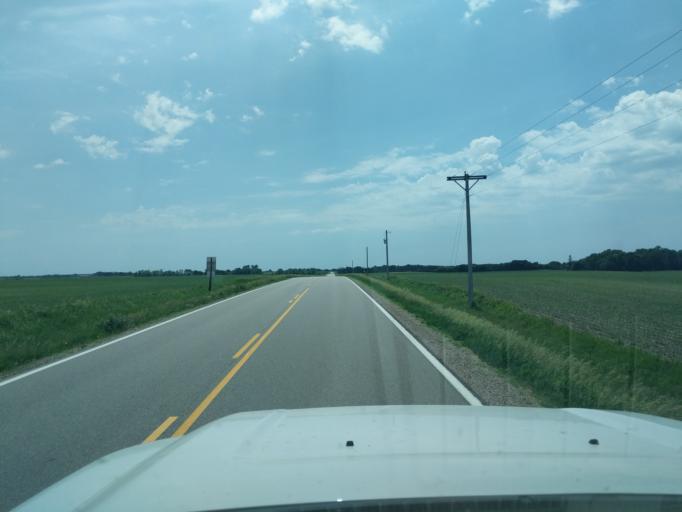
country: US
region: Minnesota
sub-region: Yellow Medicine County
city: Granite Falls
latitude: 44.7596
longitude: -95.4015
